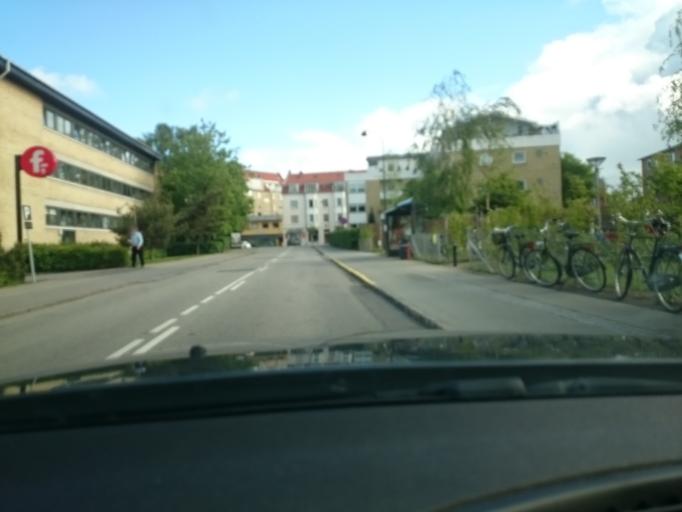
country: DK
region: Capital Region
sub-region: Gentofte Kommune
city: Charlottenlund
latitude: 55.7602
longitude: 12.5746
